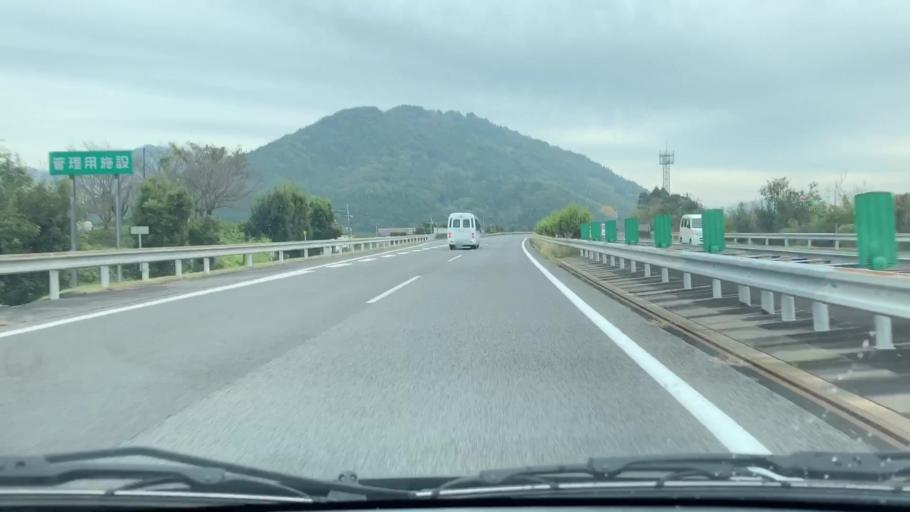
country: JP
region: Saga Prefecture
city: Takeocho-takeo
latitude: 33.2676
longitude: 130.0897
